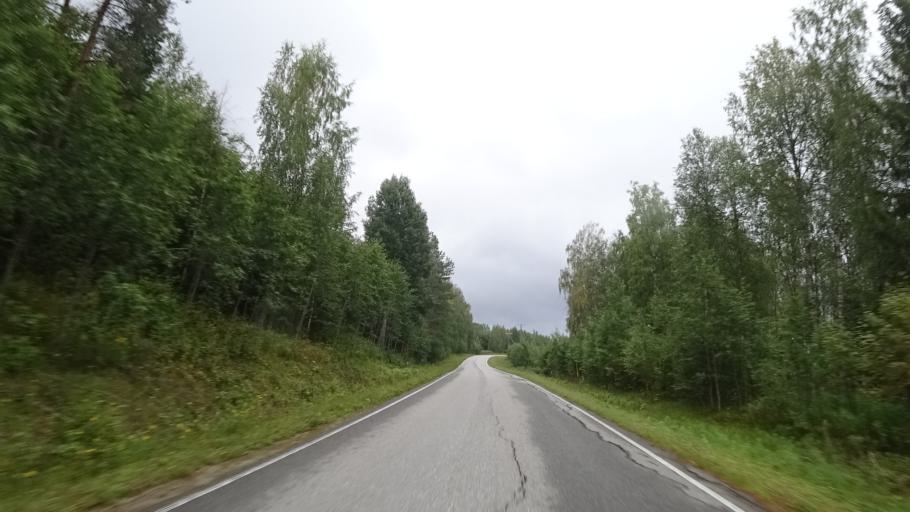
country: FI
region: North Karelia
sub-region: Joensuu
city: Ilomantsi
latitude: 63.2477
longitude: 30.7613
